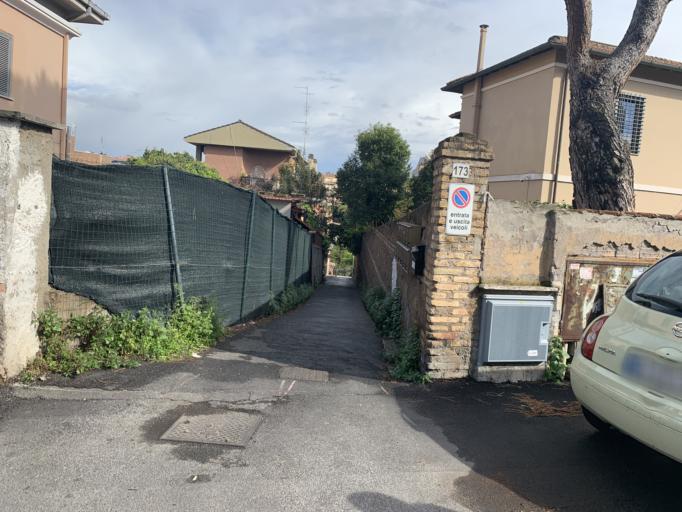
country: VA
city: Vatican City
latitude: 41.8795
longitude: 12.4190
